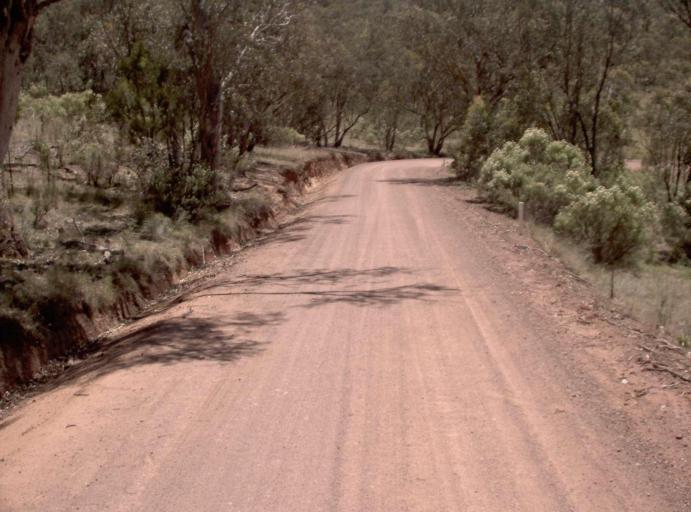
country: AU
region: New South Wales
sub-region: Snowy River
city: Jindabyne
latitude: -36.9364
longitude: 148.3441
